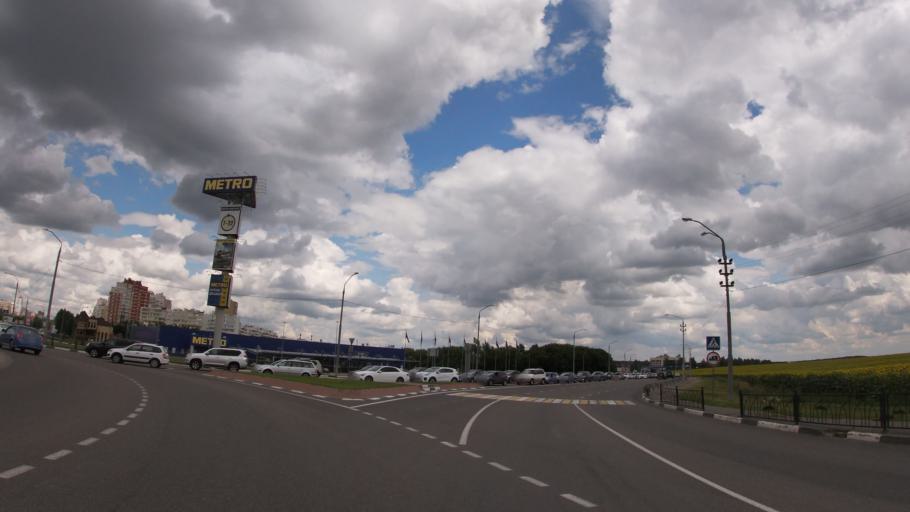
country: RU
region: Belgorod
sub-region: Belgorodskiy Rayon
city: Belgorod
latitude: 50.5512
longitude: 36.5734
